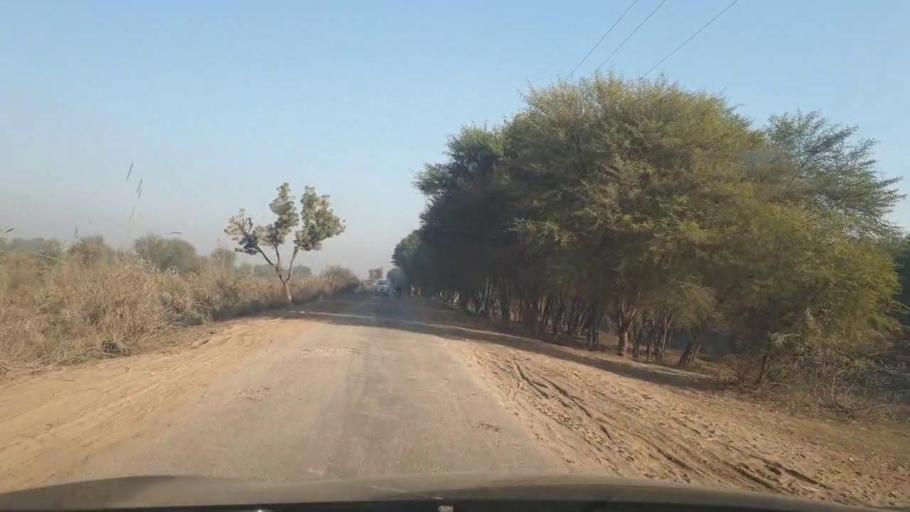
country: PK
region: Sindh
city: Mirpur Mathelo
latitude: 28.0652
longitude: 69.4652
